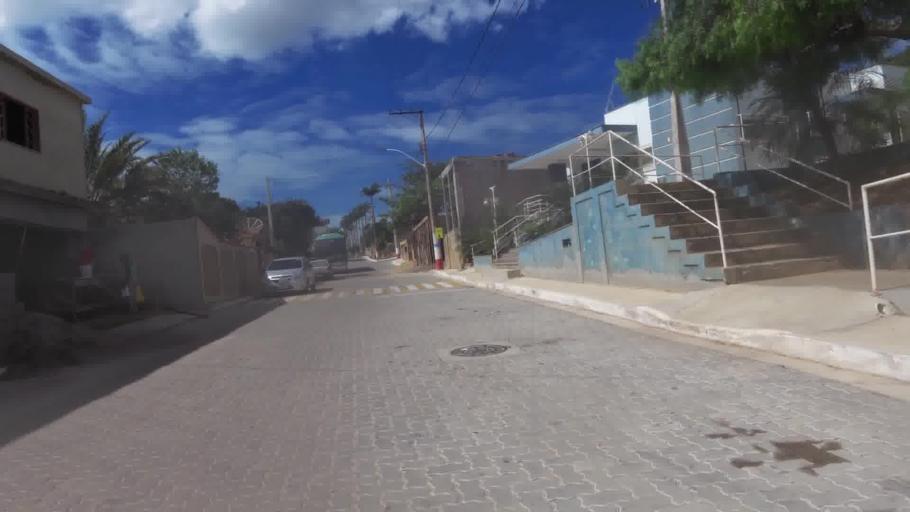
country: BR
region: Espirito Santo
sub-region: Marataizes
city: Marataizes
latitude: -21.1797
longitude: -40.9865
